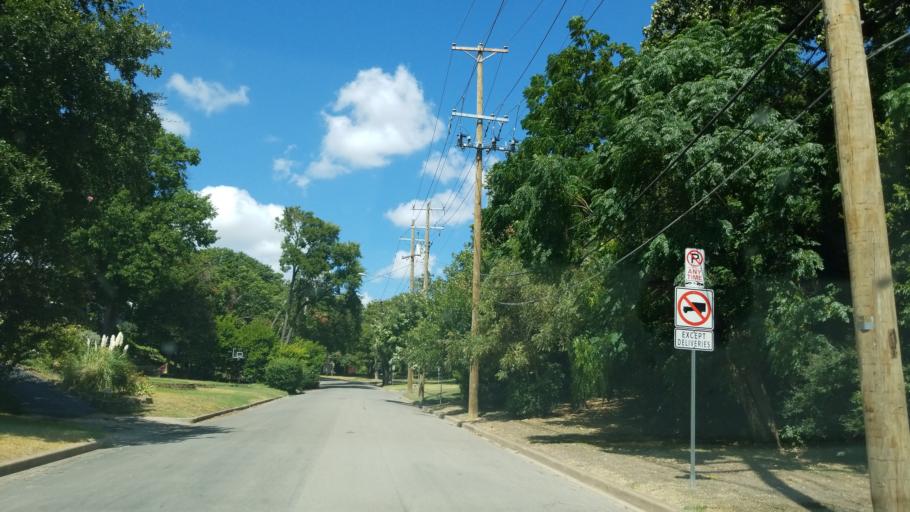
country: US
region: Texas
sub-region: Dallas County
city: Dallas
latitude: 32.7632
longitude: -96.8249
